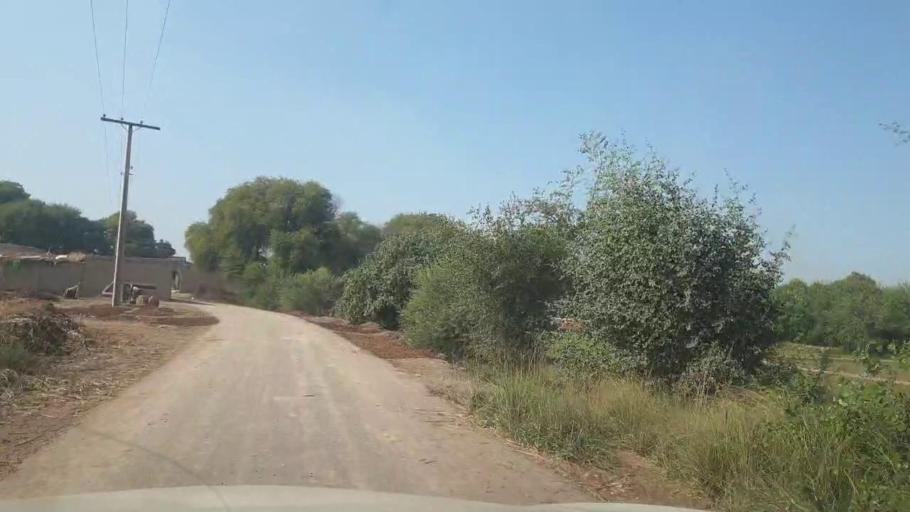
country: PK
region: Sindh
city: Bhan
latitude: 26.5840
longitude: 67.6996
